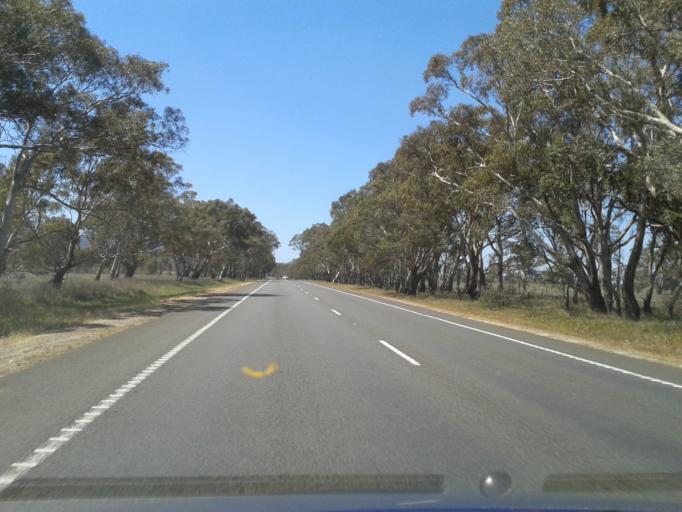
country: AU
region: Victoria
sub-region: Ararat
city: Ararat
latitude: -37.3167
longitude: 143.0414
